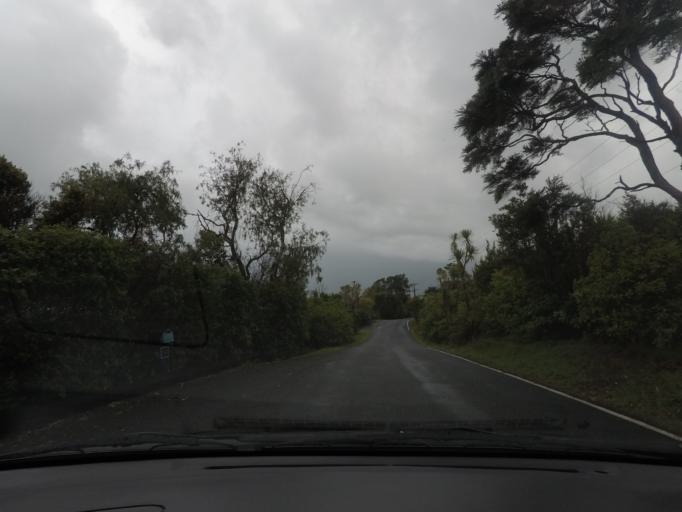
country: NZ
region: Auckland
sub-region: Auckland
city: Warkworth
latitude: -36.4798
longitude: 174.7291
